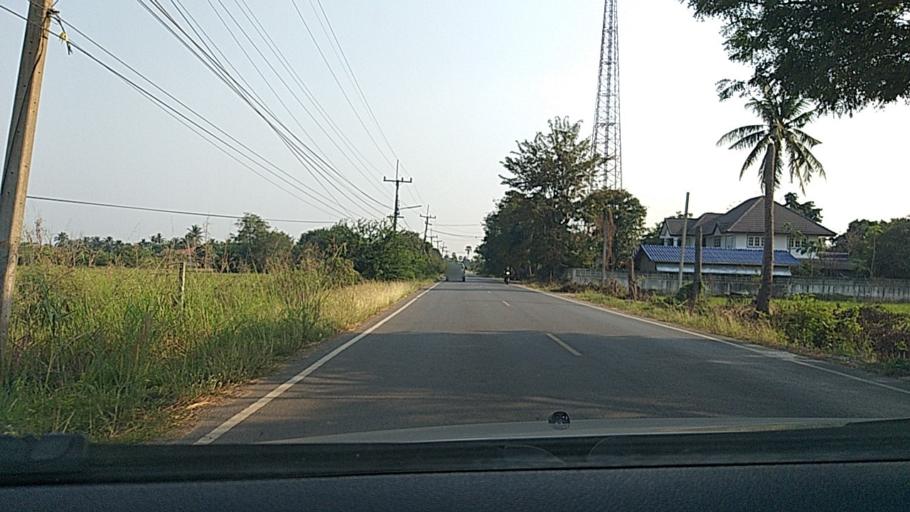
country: TH
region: Sing Buri
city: Sing Buri
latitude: 14.8455
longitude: 100.3919
